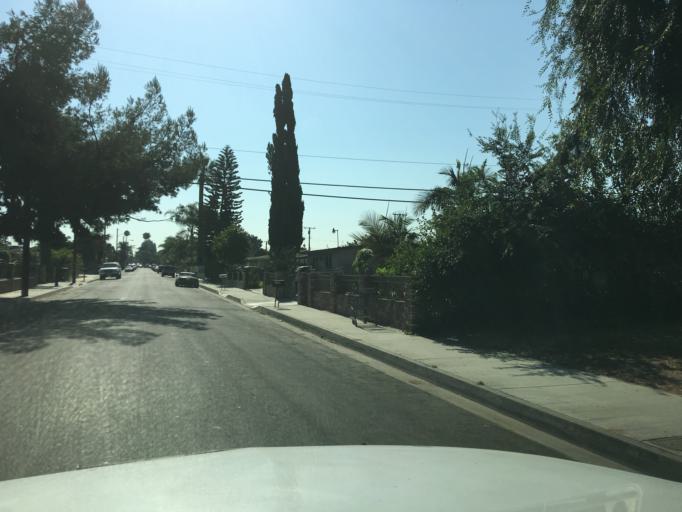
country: US
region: California
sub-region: Los Angeles County
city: Citrus
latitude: 34.1094
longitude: -117.9043
